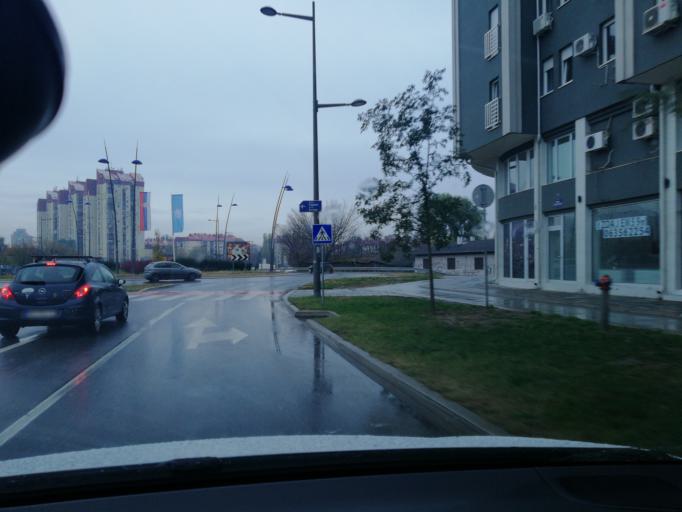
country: RS
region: Autonomna Pokrajina Vojvodina
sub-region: Juznobacki Okrug
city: Novi Sad
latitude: 45.2396
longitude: 19.8220
